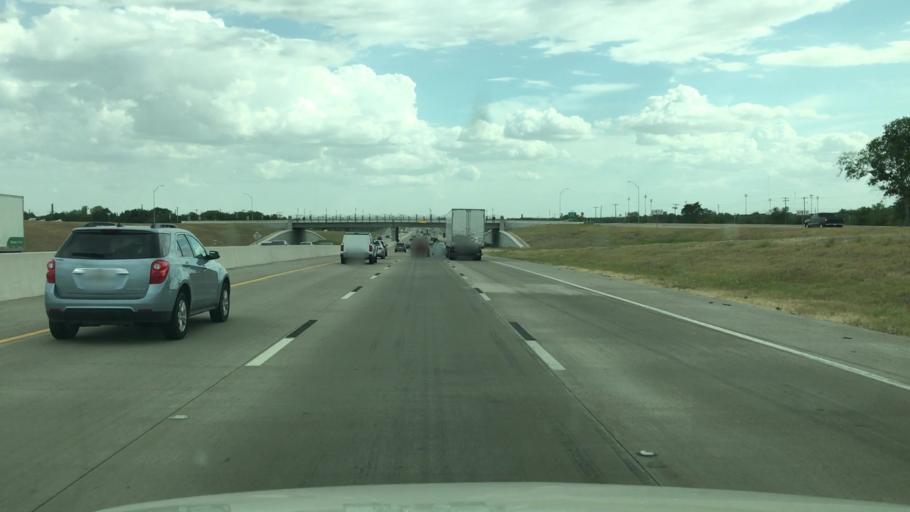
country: US
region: Texas
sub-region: McLennan County
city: Lorena
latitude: 31.3830
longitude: -97.2134
